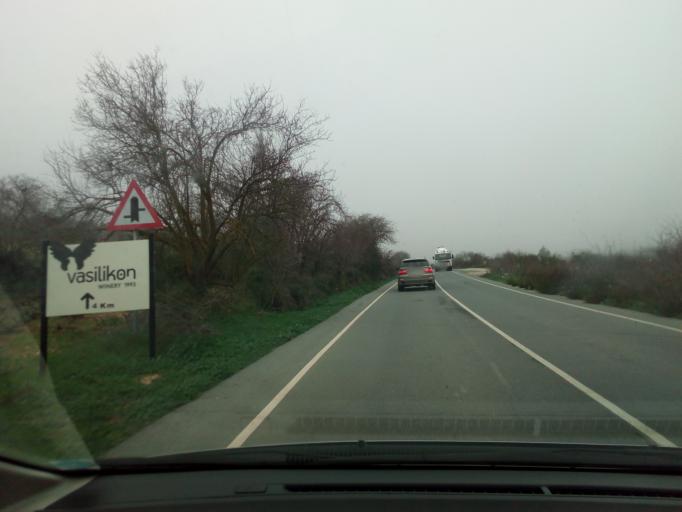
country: CY
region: Pafos
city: Pegeia
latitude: 34.9084
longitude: 32.4374
